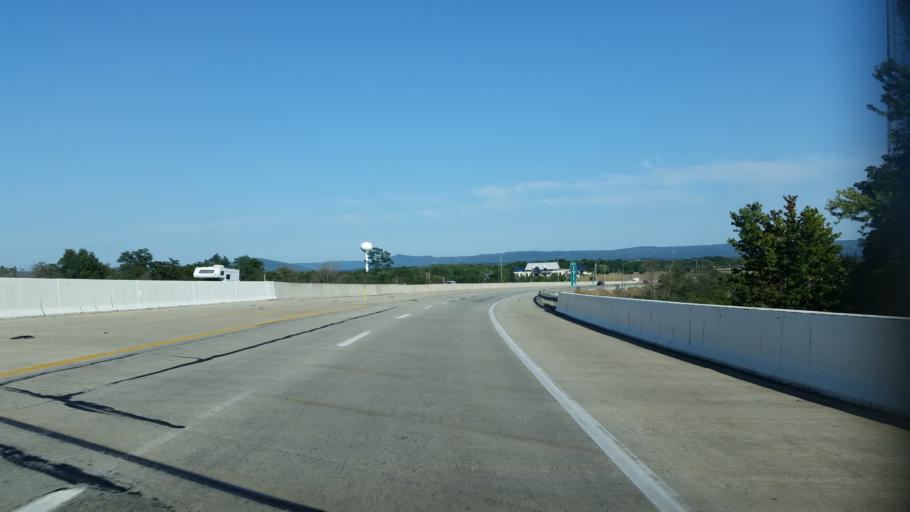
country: US
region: Pennsylvania
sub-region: Fulton County
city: McConnellsburg
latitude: 40.0599
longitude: -78.0913
